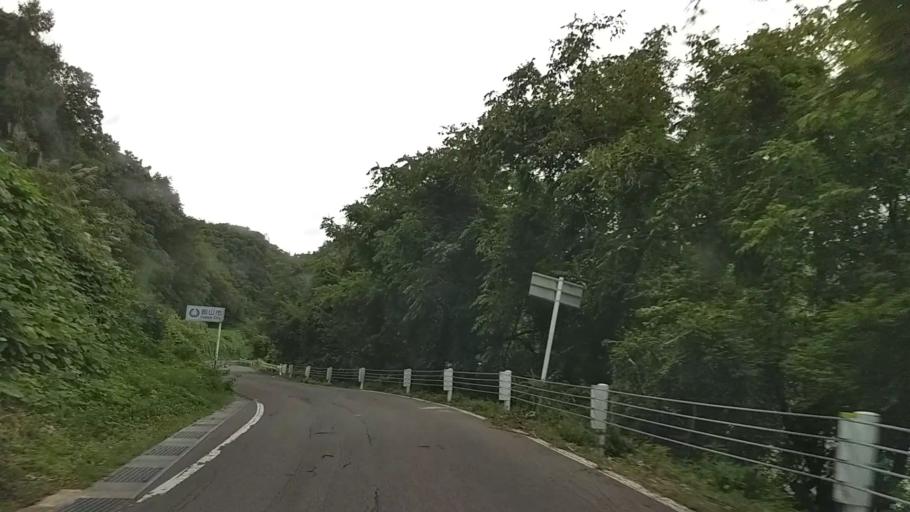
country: JP
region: Nagano
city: Iiyama
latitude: 36.8033
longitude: 138.3440
